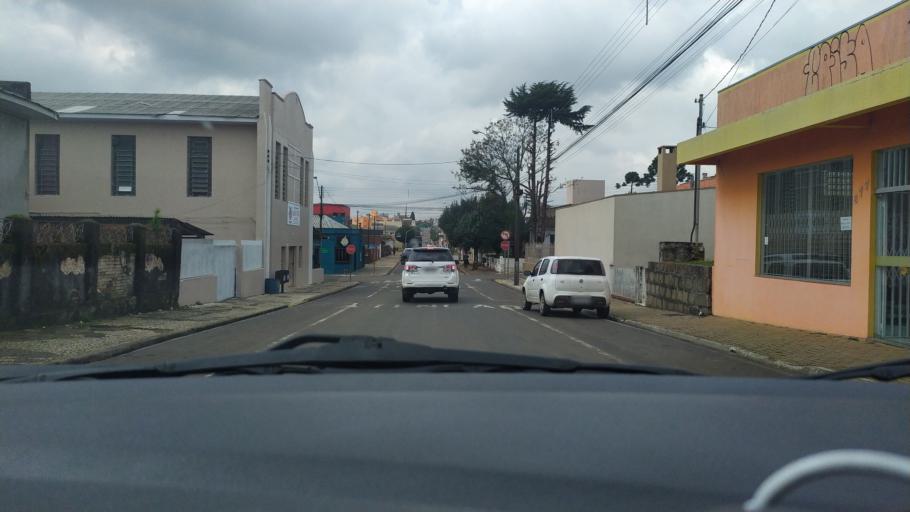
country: BR
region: Parana
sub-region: Palmas
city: Palmas
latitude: -26.4831
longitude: -51.9884
